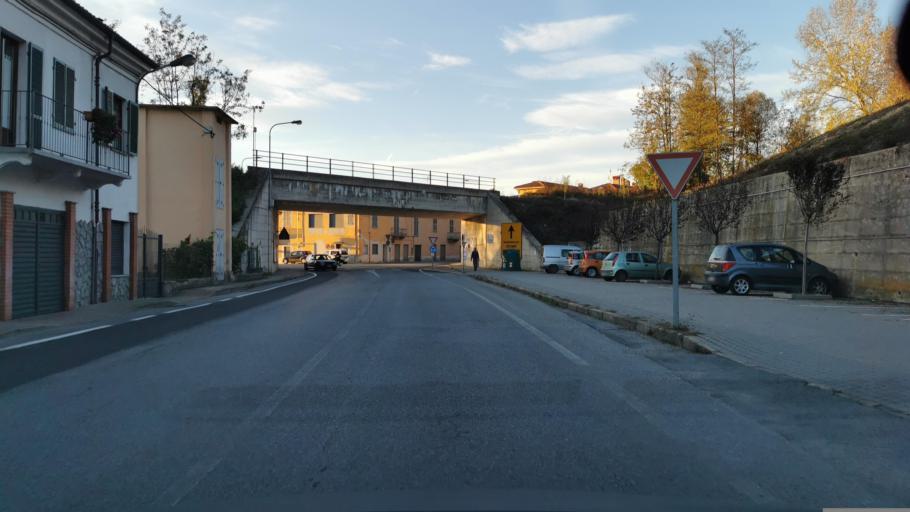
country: IT
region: Piedmont
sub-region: Provincia di Cuneo
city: Monchiero Borgonuovo
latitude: 44.5684
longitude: 7.9182
